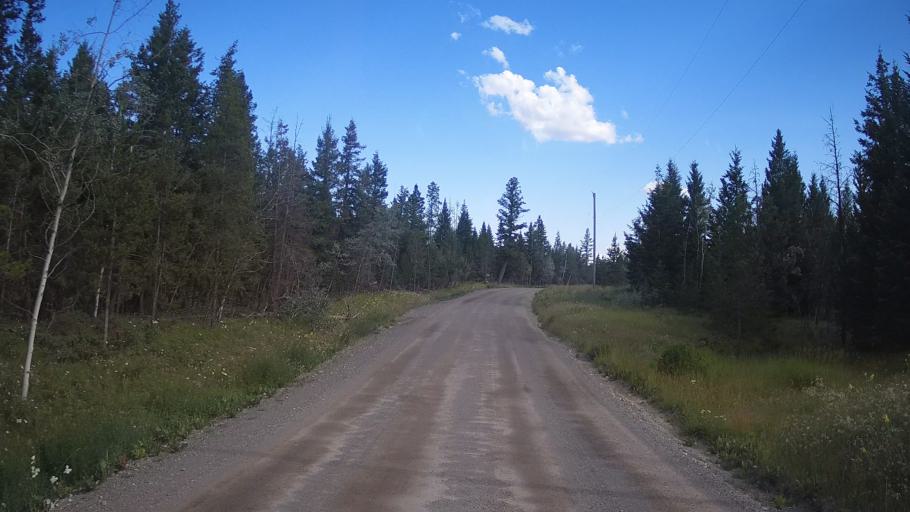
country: CA
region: British Columbia
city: Cache Creek
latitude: 51.1875
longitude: -121.5849
